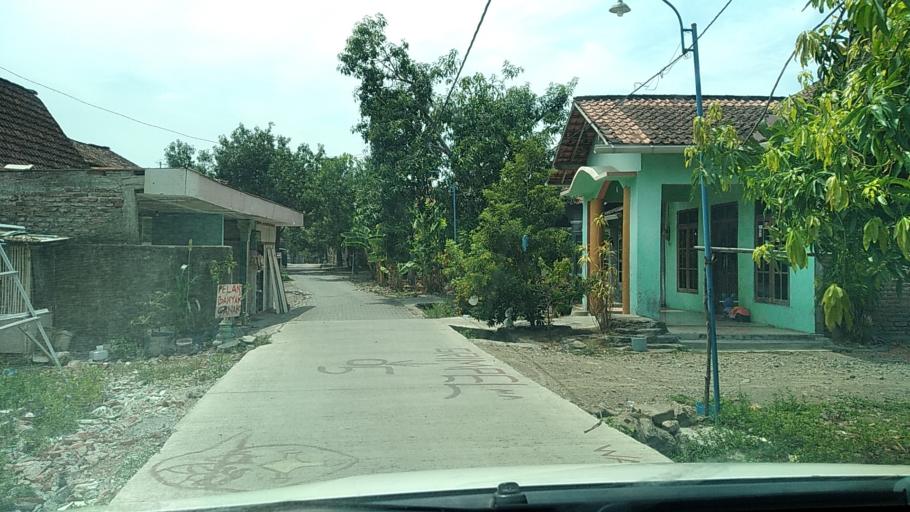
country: ID
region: Central Java
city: Mranggen
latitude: -7.0572
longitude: 110.4781
